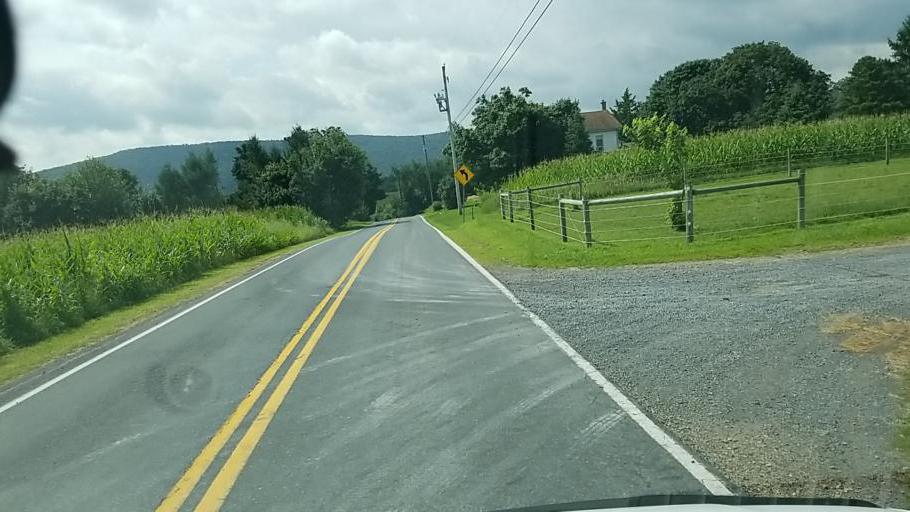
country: US
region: Pennsylvania
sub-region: Dauphin County
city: Millersburg
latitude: 40.5549
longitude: -76.8917
